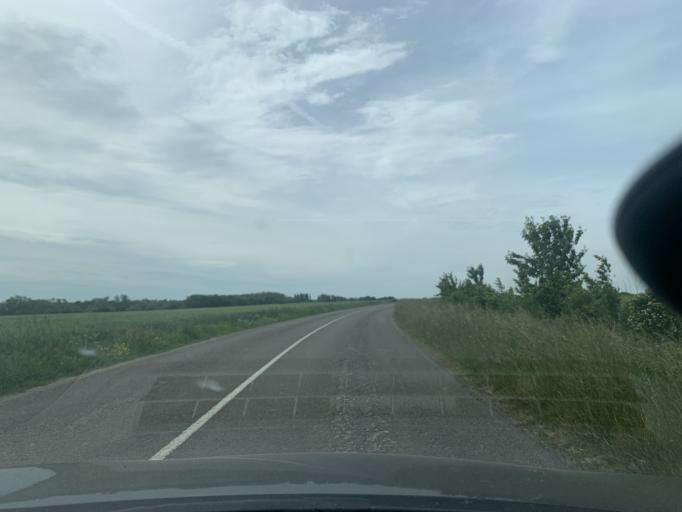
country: FR
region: Nord-Pas-de-Calais
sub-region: Departement du Nord
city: Marcoing
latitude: 50.1329
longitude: 3.1833
